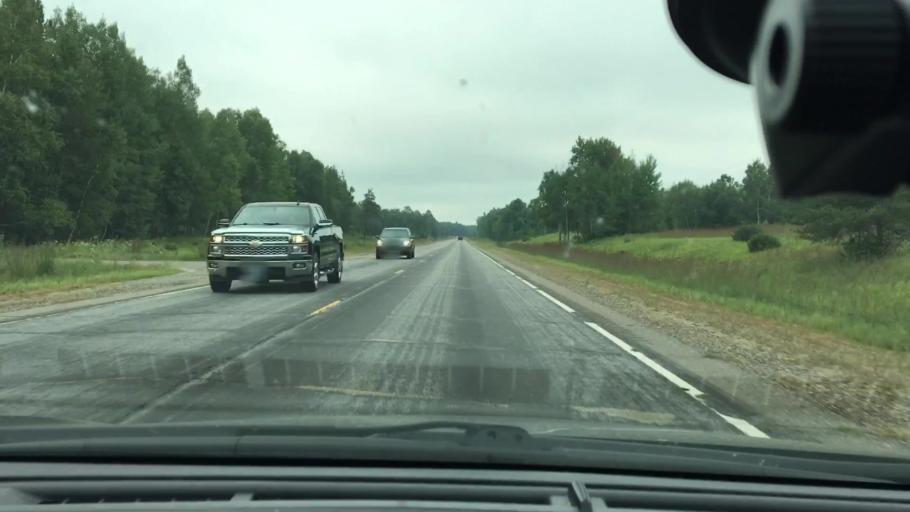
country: US
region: Minnesota
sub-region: Crow Wing County
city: Cross Lake
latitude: 46.6812
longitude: -93.9532
